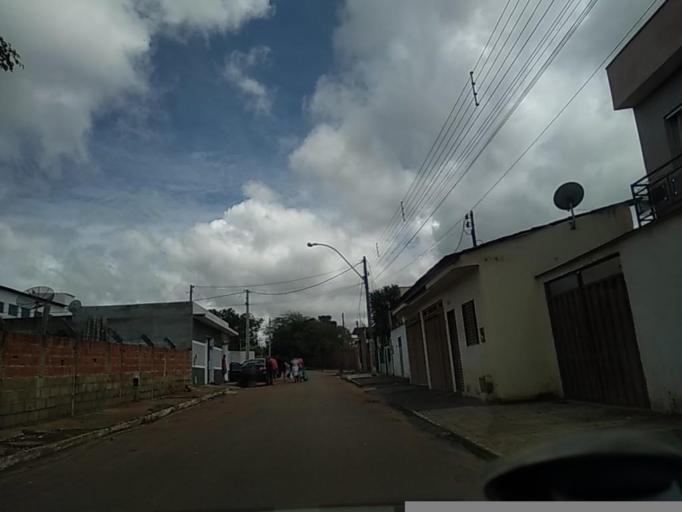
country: BR
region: Bahia
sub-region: Caetite
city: Caetite
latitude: -14.0553
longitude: -42.4830
